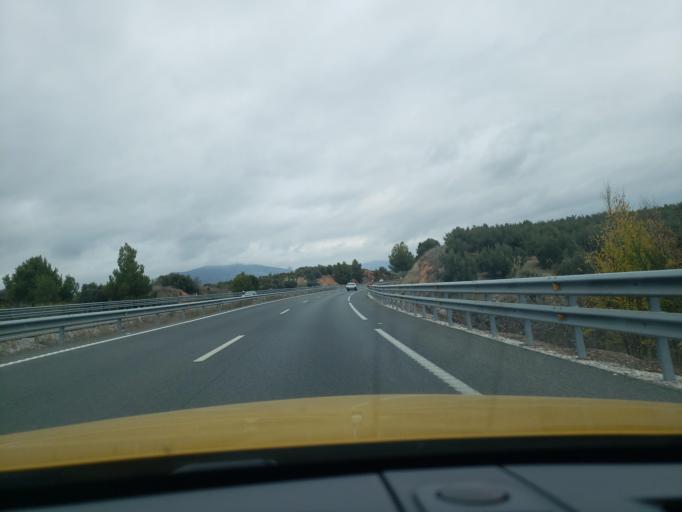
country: ES
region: Andalusia
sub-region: Provincia de Granada
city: Calicasas
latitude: 37.2872
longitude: -3.6584
